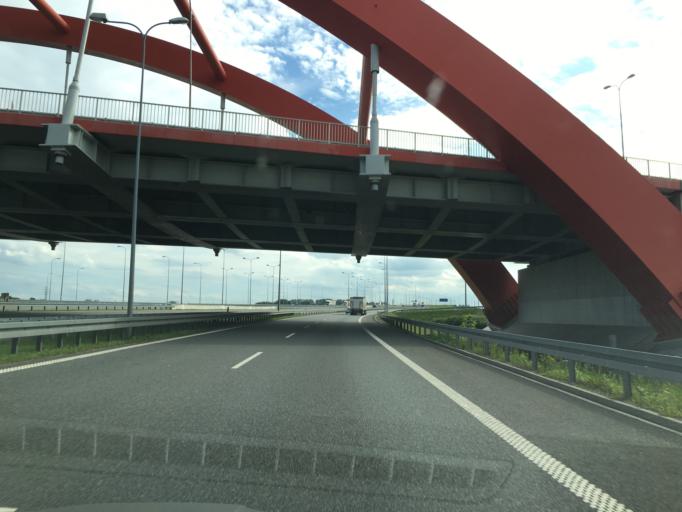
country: PL
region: Silesian Voivodeship
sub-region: Powiat gliwicki
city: Przyszowice
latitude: 50.2693
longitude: 18.7283
